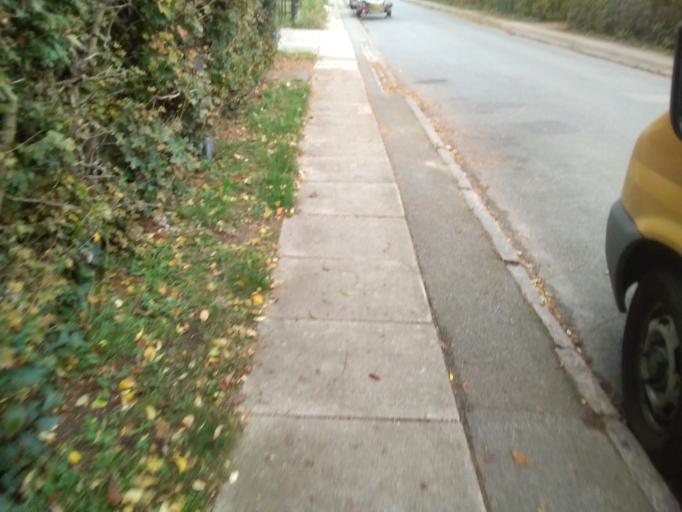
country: DK
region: Capital Region
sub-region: Rodovre Kommune
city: Rodovre
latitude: 55.7069
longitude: 12.4651
